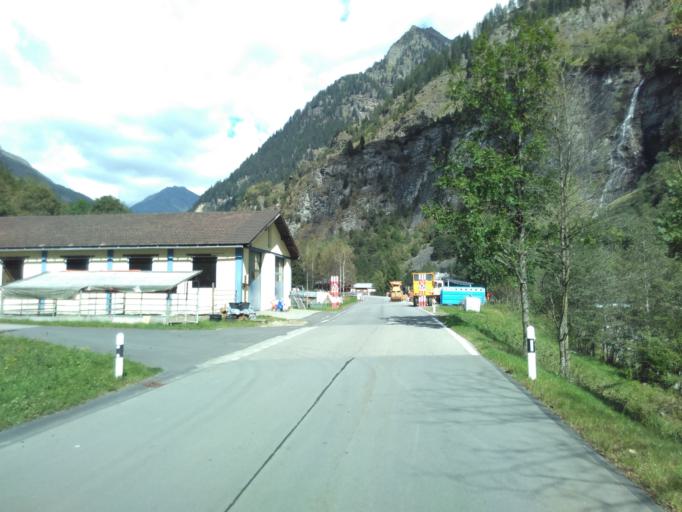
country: CH
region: Grisons
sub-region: Moesa District
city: Cauco
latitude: 46.3607
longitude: 9.1268
